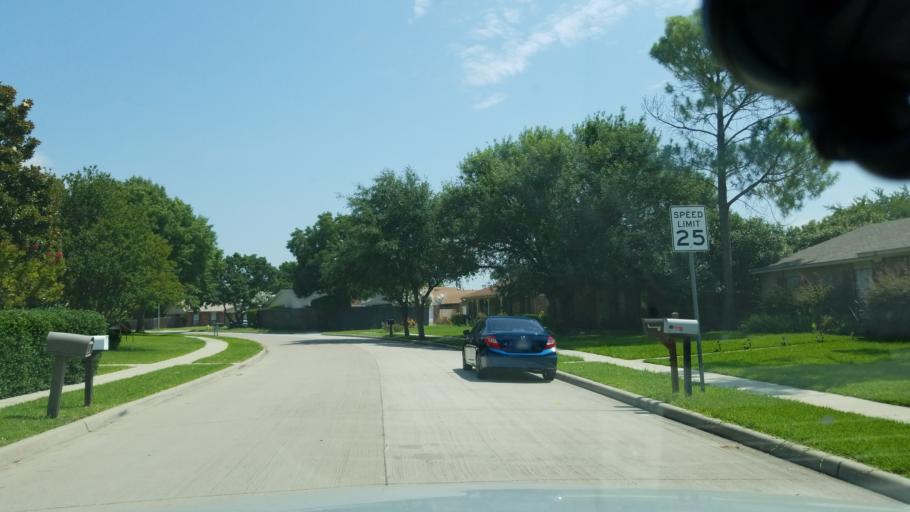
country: US
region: Texas
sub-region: Dallas County
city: Coppell
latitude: 32.9633
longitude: -96.9876
